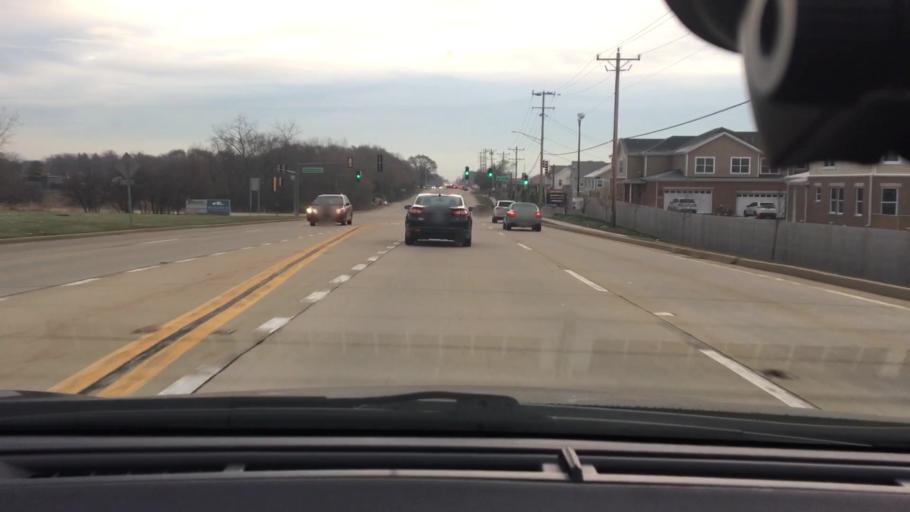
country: US
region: Illinois
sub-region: Lake County
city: Kildeer
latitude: 42.1538
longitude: -88.0460
